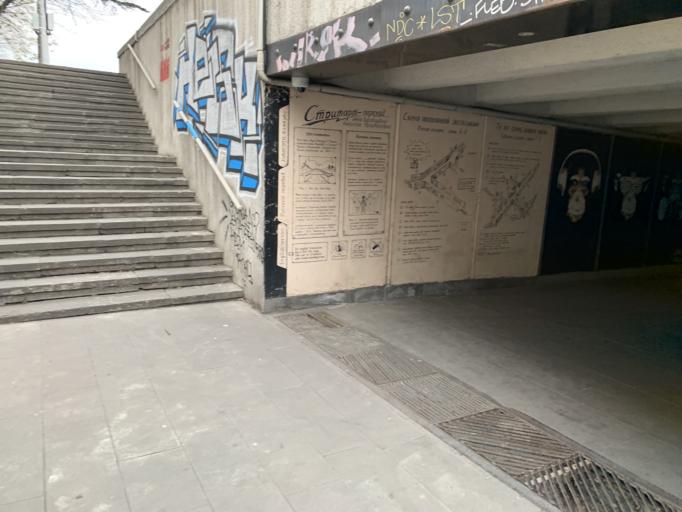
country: GE
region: T'bilisi
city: Tbilisi
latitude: 41.6971
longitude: 44.8097
